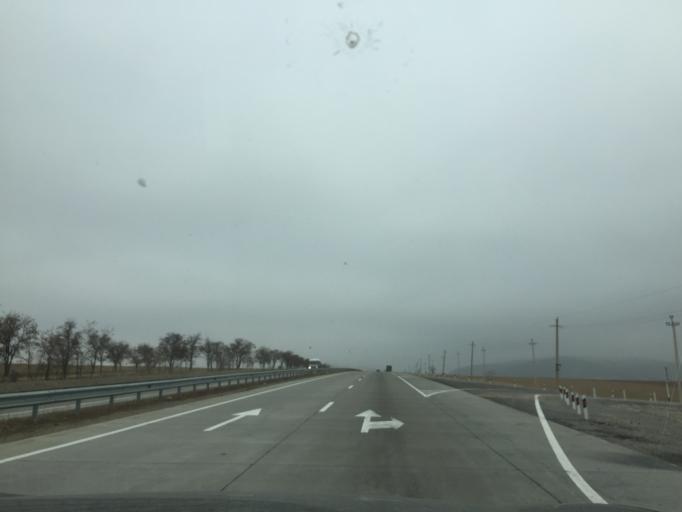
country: KZ
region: Ongtustik Qazaqstan
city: Sastobe
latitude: 42.5197
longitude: 69.9962
